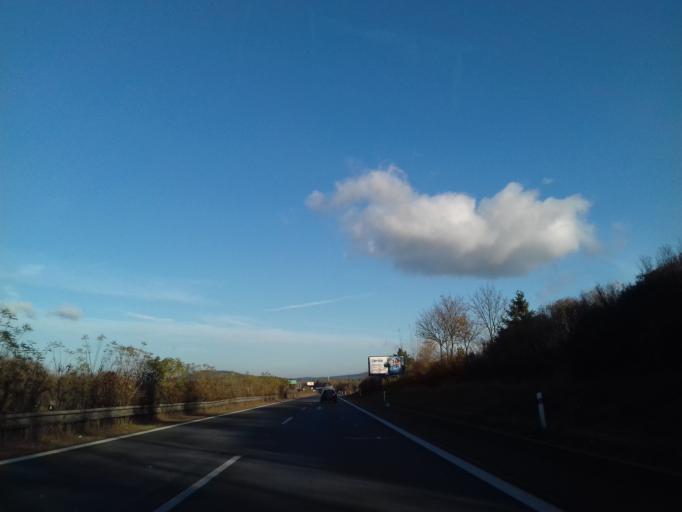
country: CZ
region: Plzensky
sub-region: Okres Rokycany
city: Rokycany
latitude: 49.7556
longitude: 13.6043
